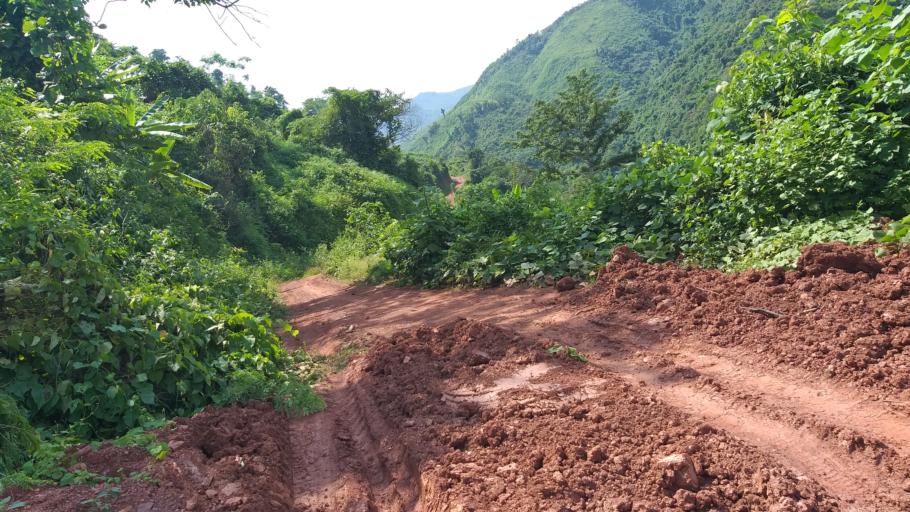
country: LA
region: Phongsali
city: Khoa
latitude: 21.2929
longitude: 102.5446
